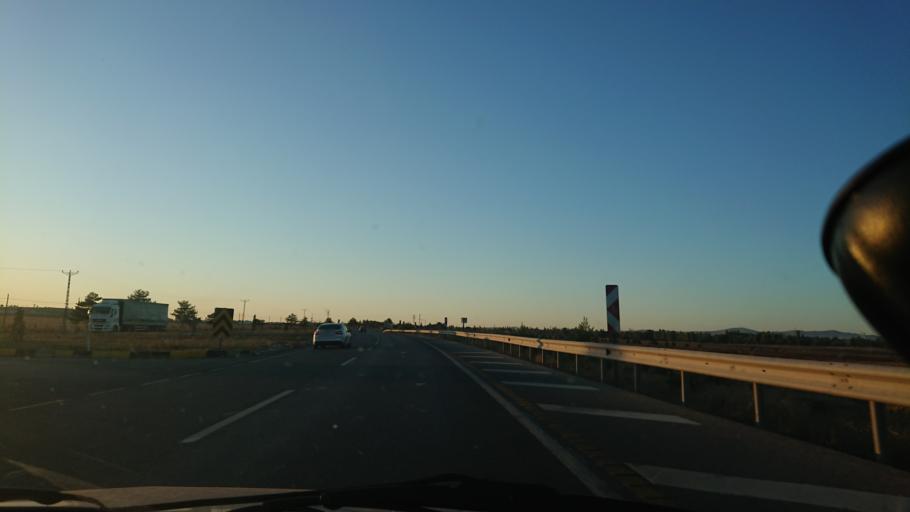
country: TR
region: Eskisehir
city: Mahmudiye
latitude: 39.5552
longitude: 30.9225
